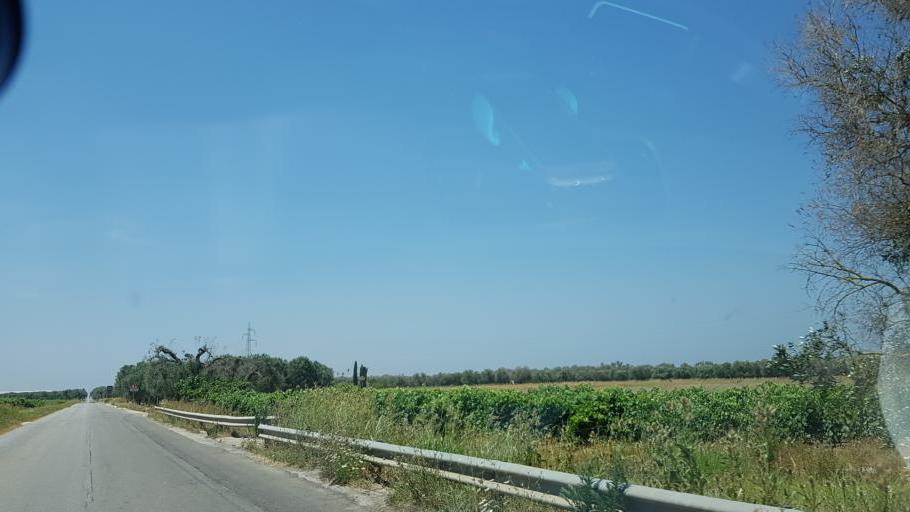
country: IT
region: Apulia
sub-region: Provincia di Brindisi
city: San Donaci
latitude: 40.4630
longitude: 17.9075
